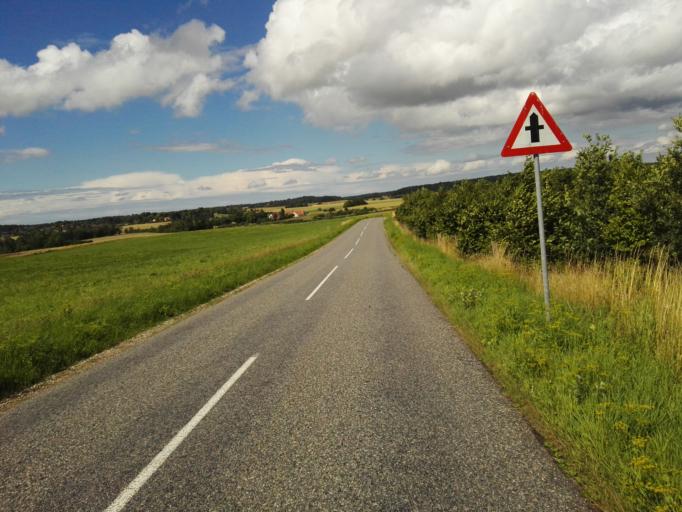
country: DK
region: Capital Region
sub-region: Egedal Kommune
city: Ganlose
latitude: 55.7857
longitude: 12.2341
